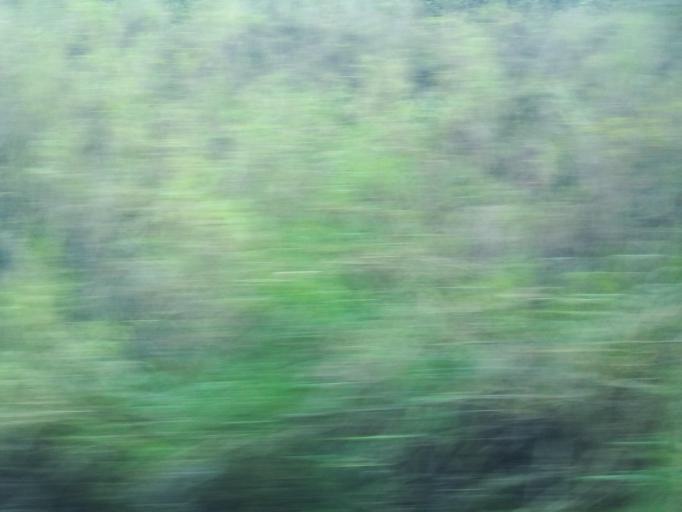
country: BR
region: Minas Gerais
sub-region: Rio Piracicaba
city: Rio Piracicaba
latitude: -19.8908
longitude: -43.1392
